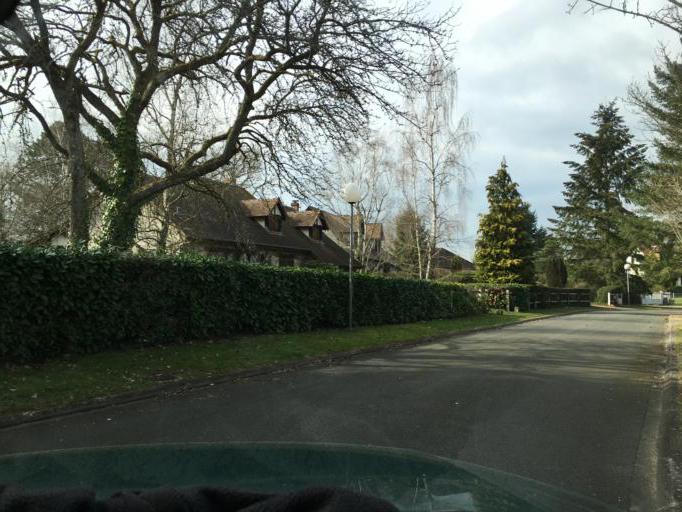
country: FR
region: Centre
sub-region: Departement du Loiret
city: Jouy-le-Potier
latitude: 47.7742
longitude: 1.8684
